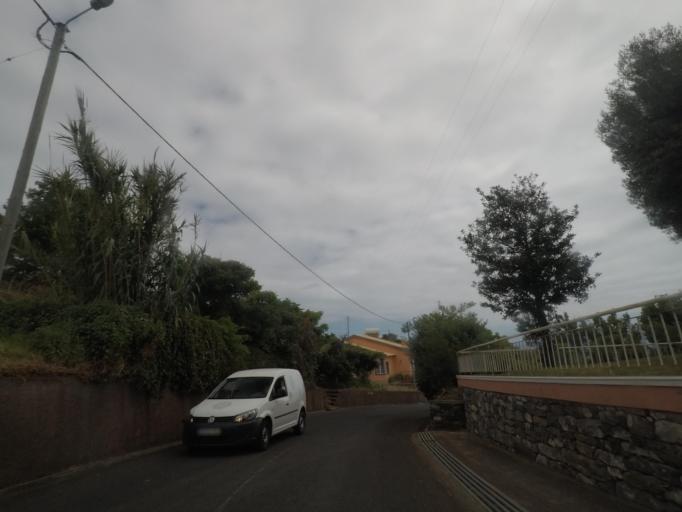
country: PT
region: Madeira
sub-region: Calheta
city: Estreito da Calheta
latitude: 32.7331
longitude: -17.1740
